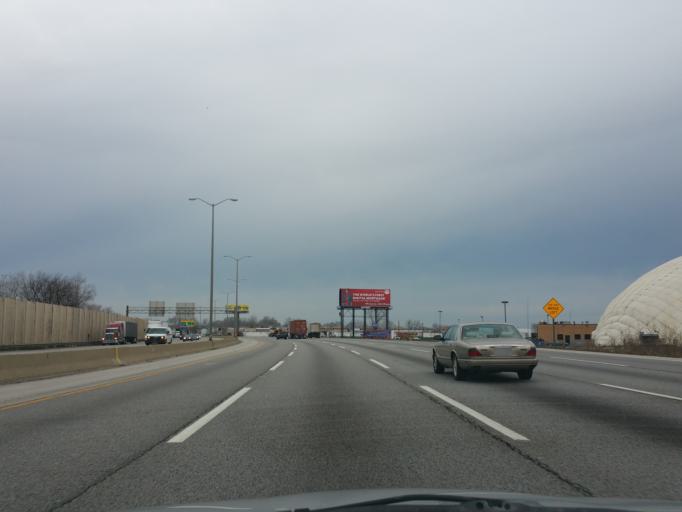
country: US
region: Illinois
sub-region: Cook County
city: Hickory Hills
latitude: 41.7260
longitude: -87.8100
